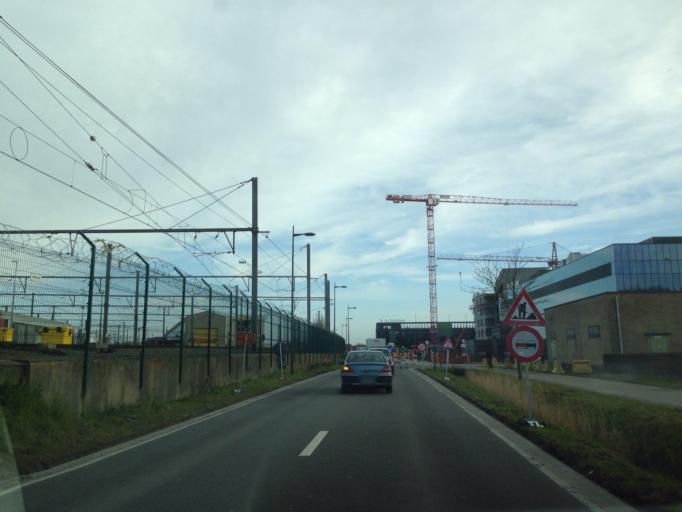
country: BE
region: Flanders
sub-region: Provincie West-Vlaanderen
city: Ostend
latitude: 51.2205
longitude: 2.9330
